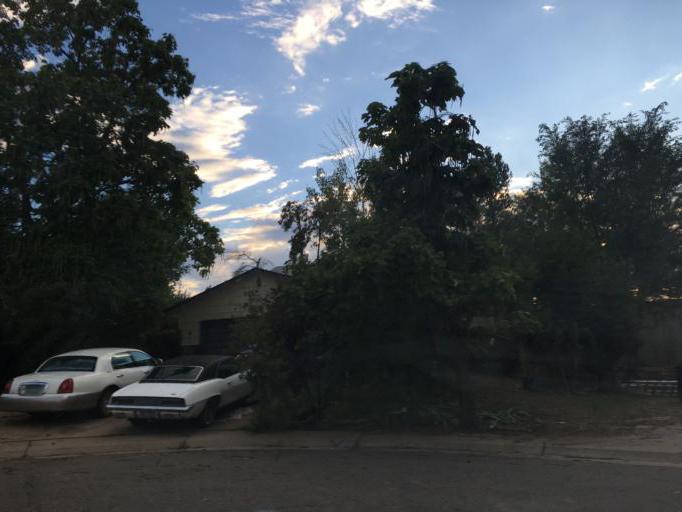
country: US
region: Colorado
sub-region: Adams County
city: Aurora
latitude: 39.6791
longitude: -104.8642
